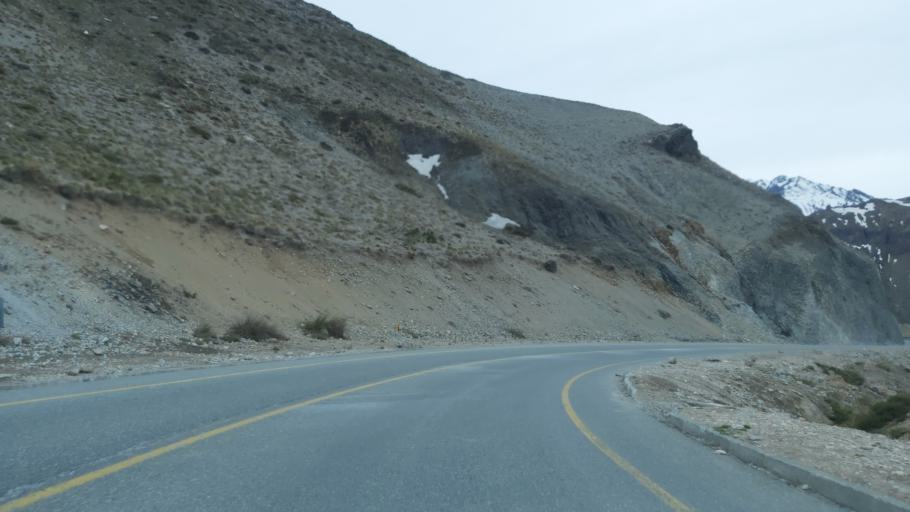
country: CL
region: Maule
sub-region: Provincia de Linares
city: Colbun
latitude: -35.9617
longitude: -70.5738
